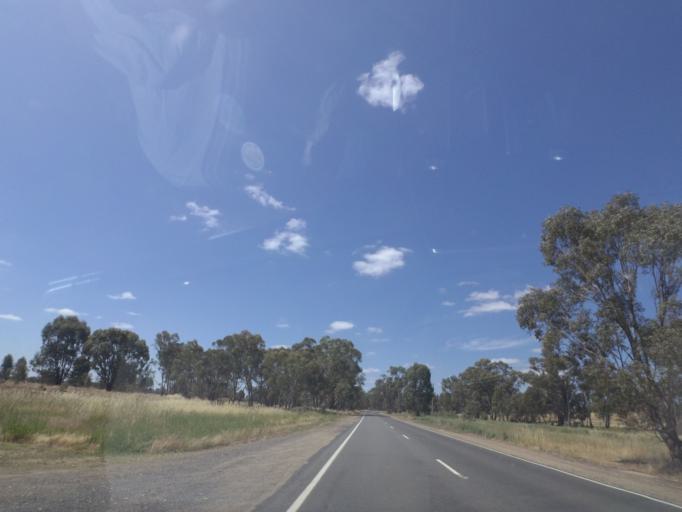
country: AU
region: Victoria
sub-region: Wangaratta
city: Wangaratta
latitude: -36.4092
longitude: 146.2703
